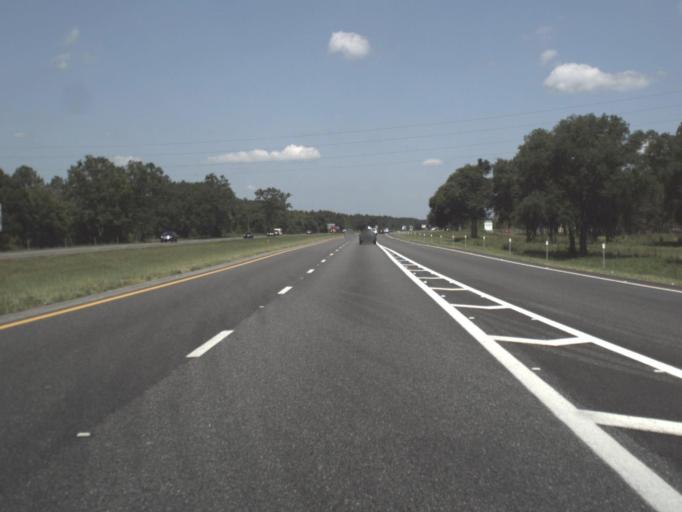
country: US
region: Florida
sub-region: Madison County
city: Madison
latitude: 30.3808
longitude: -83.3018
